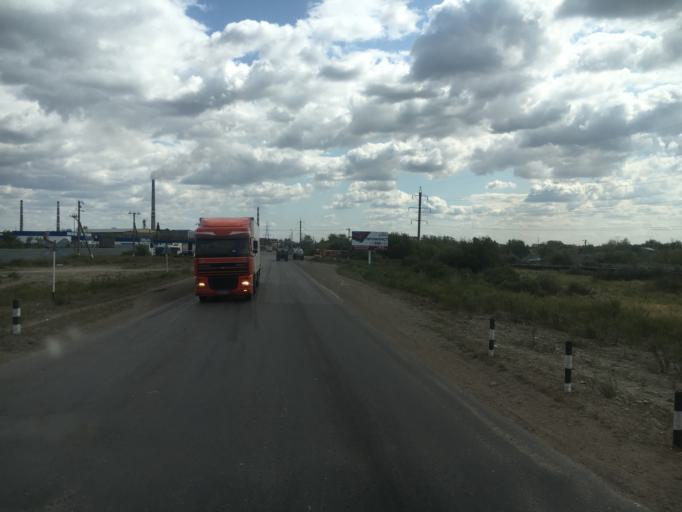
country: KZ
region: Qostanay
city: Rudnyy
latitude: 52.9857
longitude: 63.1050
